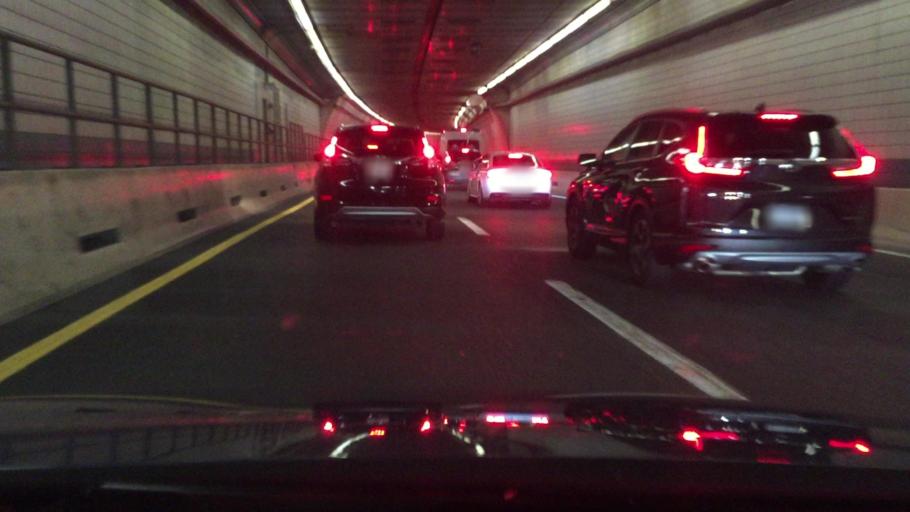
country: US
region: Massachusetts
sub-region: Suffolk County
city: Boston
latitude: 42.3600
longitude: -71.0299
